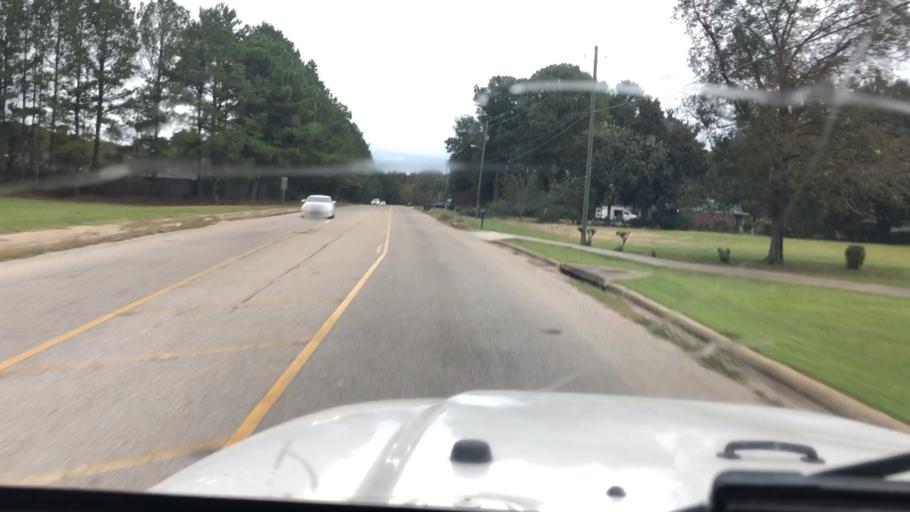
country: US
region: Alabama
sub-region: Elmore County
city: Blue Ridge
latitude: 32.4018
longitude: -86.1878
